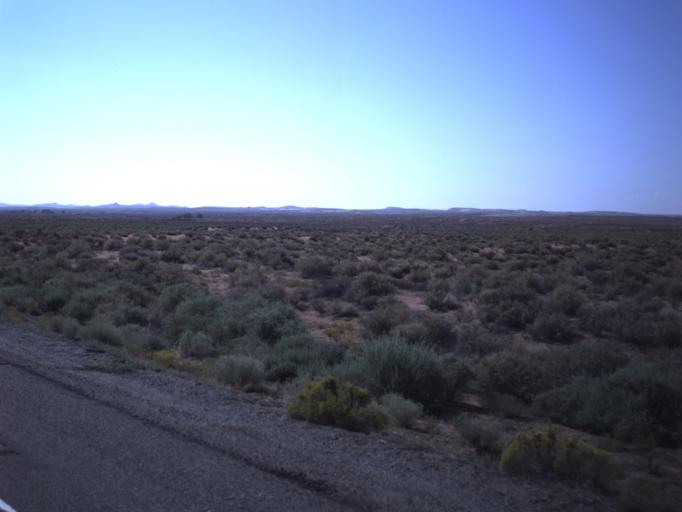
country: US
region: Utah
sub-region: San Juan County
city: Blanding
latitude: 37.1802
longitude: -109.5877
